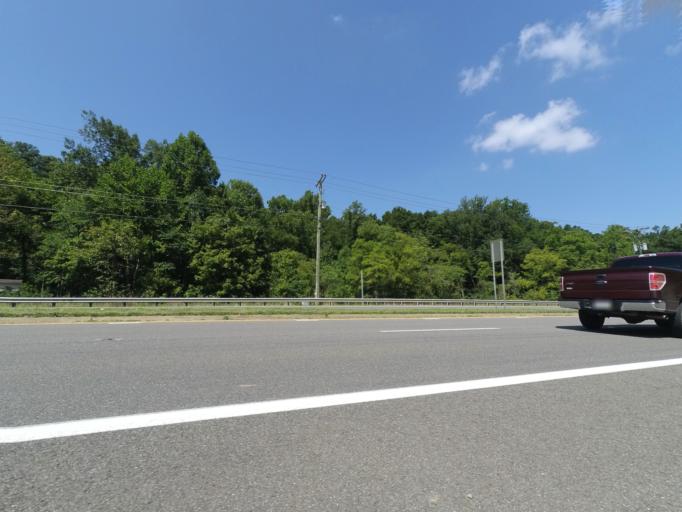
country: US
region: West Virginia
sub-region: Cabell County
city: Huntington
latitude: 38.3857
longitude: -82.4569
